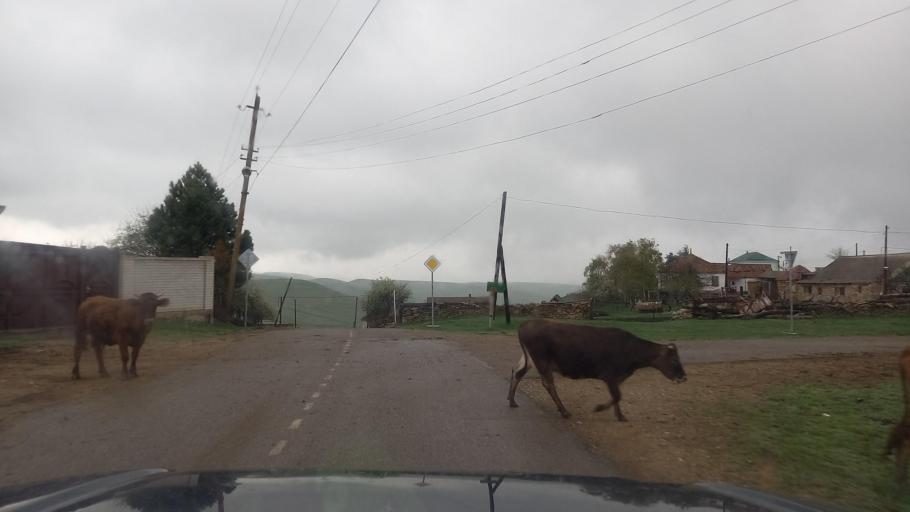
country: RU
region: Stavropol'skiy
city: Nezhinskiy
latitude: 43.8621
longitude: 42.6428
